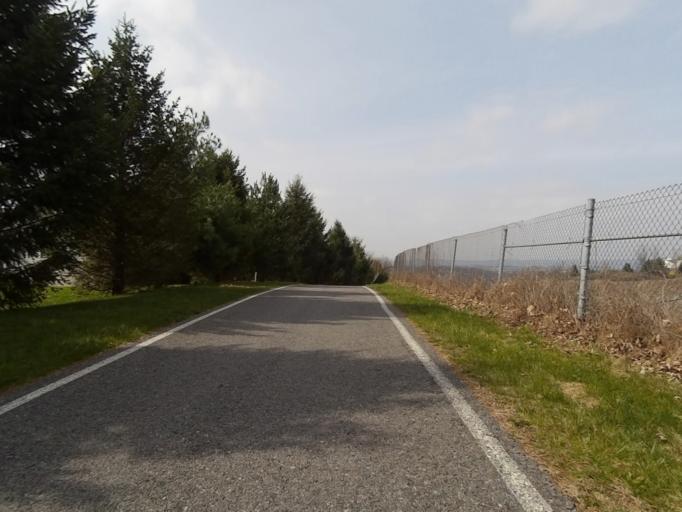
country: US
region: Pennsylvania
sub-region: Centre County
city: Lemont
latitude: 40.7960
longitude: -77.8220
